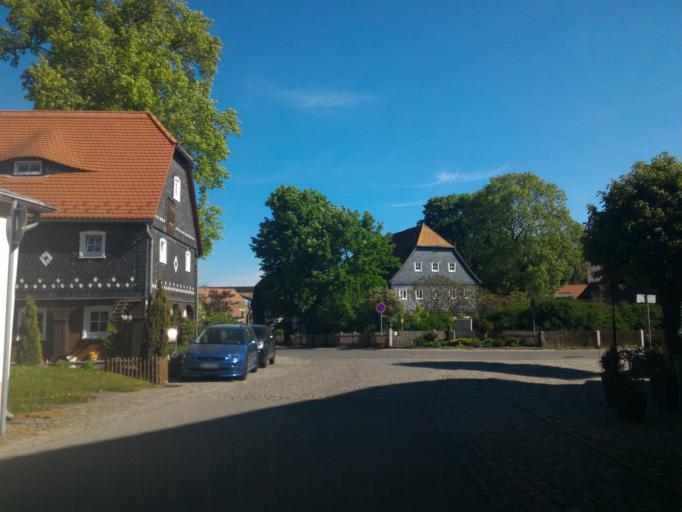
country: DE
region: Saxony
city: Niedercunnersdorf
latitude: 51.0353
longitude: 14.6680
